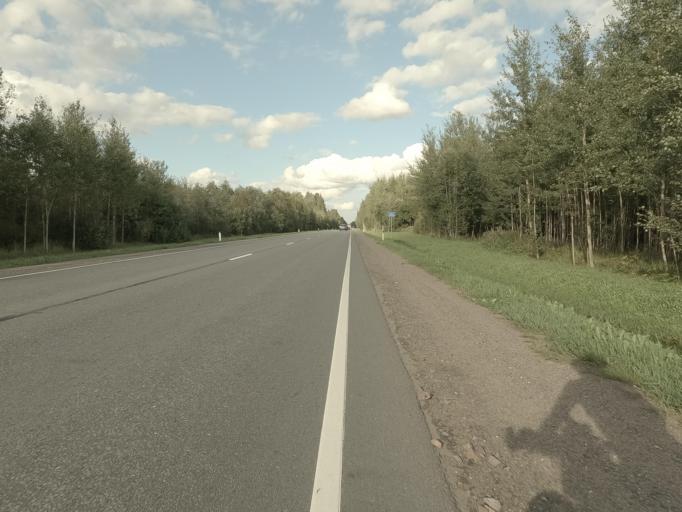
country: RU
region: Leningrad
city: Mga
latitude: 59.6863
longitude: 30.9633
